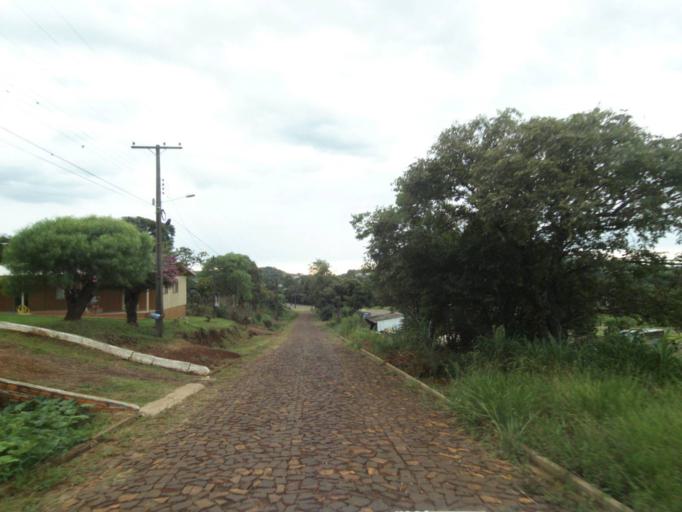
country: BR
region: Parana
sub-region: Guaraniacu
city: Guaraniacu
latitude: -25.1067
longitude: -52.8591
